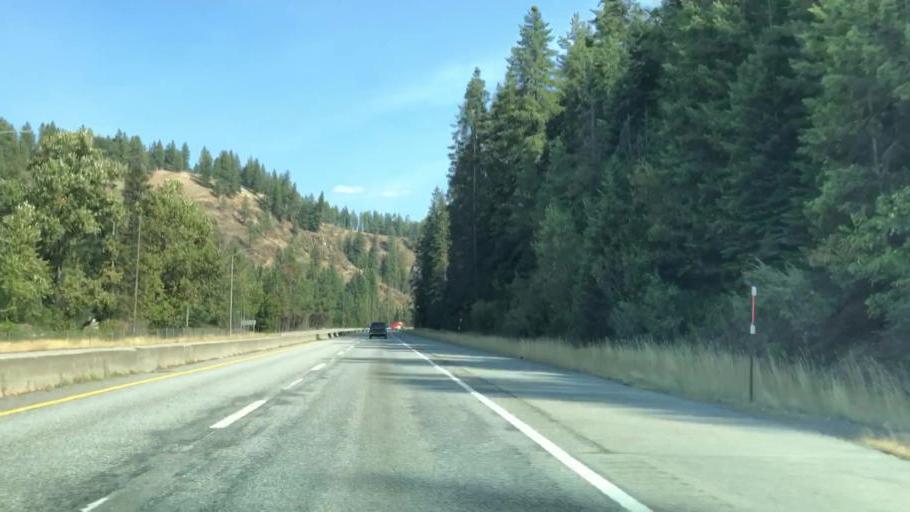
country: US
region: Idaho
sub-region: Kootenai County
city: Coeur d'Alene
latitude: 47.6305
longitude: -116.6076
